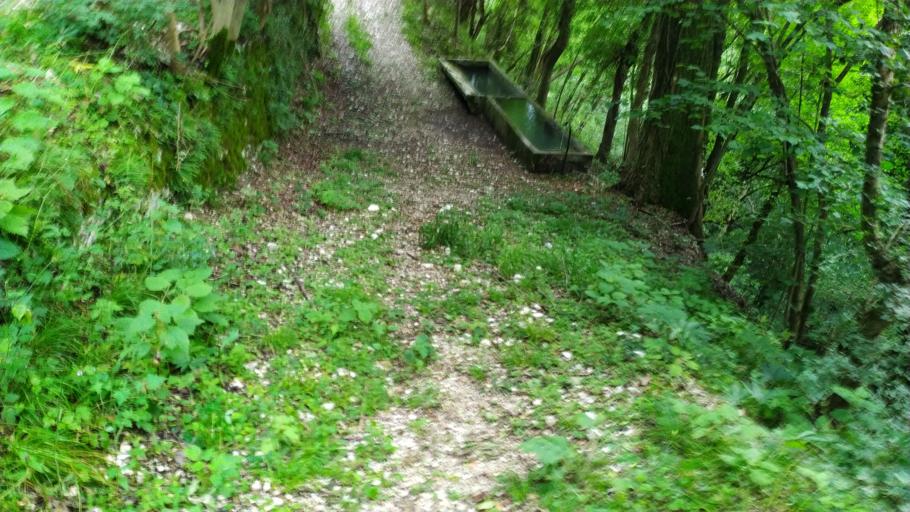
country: IT
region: Veneto
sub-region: Provincia di Vicenza
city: San Quirico
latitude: 45.6800
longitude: 11.2853
